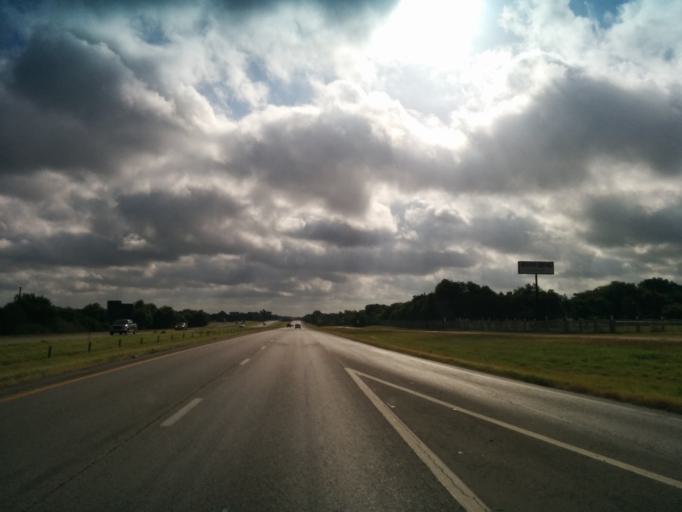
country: US
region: Texas
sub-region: Guadalupe County
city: Cibolo
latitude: 29.4986
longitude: -98.1926
